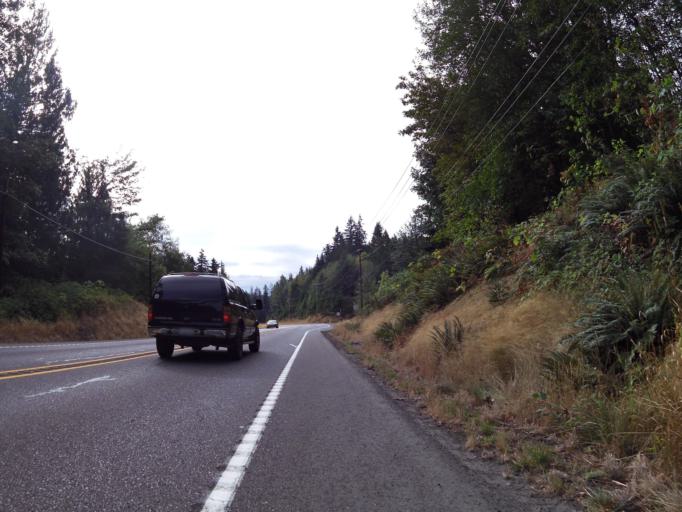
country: US
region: Washington
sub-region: Mason County
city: Allyn
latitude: 47.3999
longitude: -122.8329
